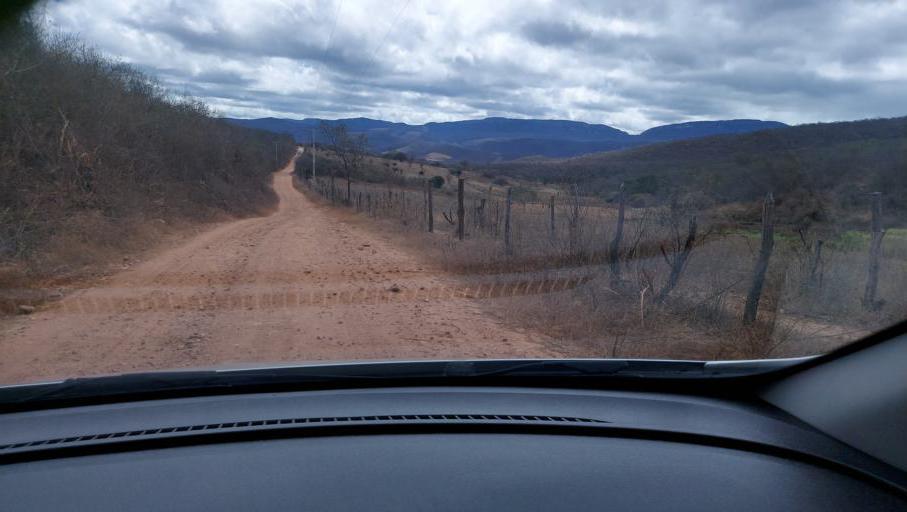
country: BR
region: Bahia
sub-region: Oliveira Dos Brejinhos
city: Beira Rio
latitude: -12.0723
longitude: -42.5397
